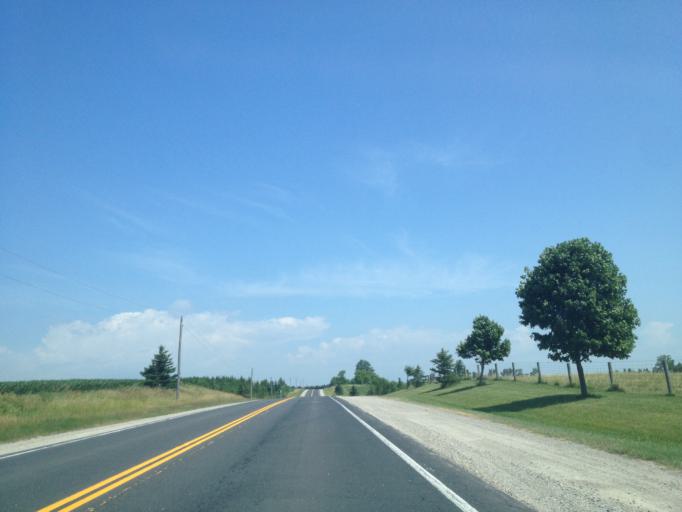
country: CA
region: Ontario
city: Huron East
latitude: 43.3936
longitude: -81.2226
